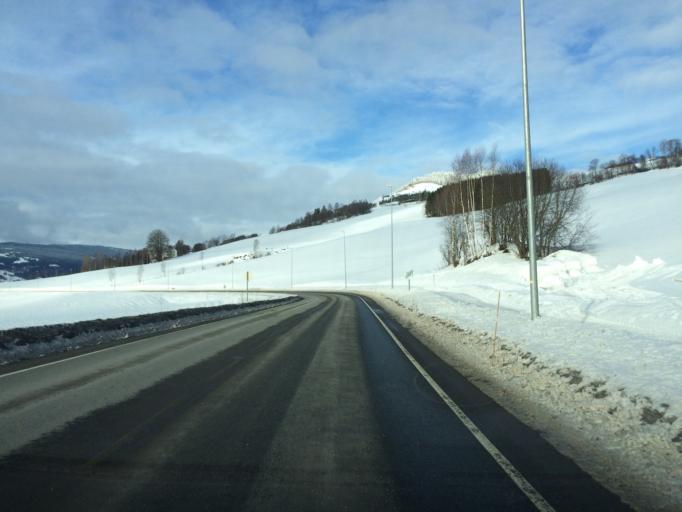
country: NO
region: Oppland
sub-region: Gausdal
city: Segalstad bru
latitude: 61.2196
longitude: 10.2697
